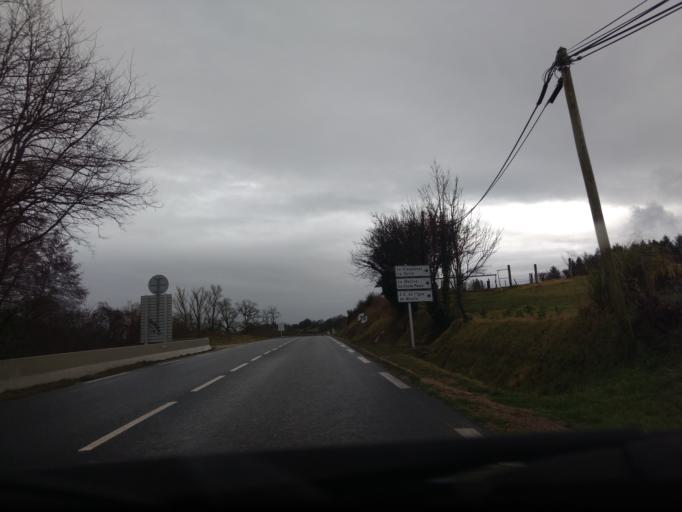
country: FR
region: Midi-Pyrenees
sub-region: Departement de l'Aveyron
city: Firmi
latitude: 44.5234
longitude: 2.3352
